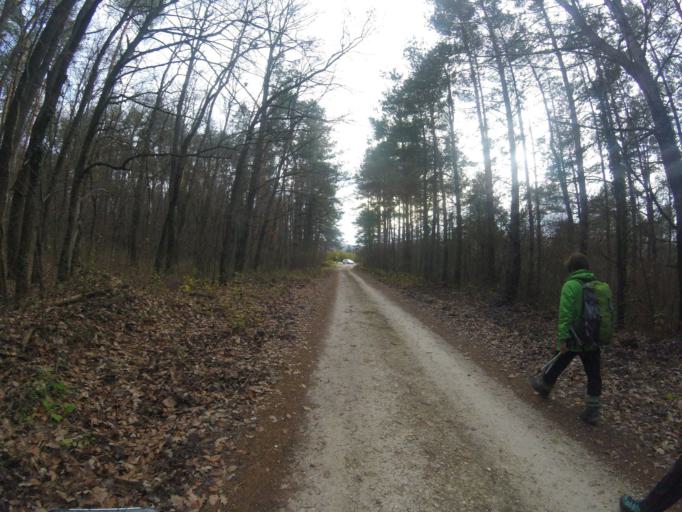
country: HU
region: Veszprem
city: Sumeg
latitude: 46.9217
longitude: 17.3335
